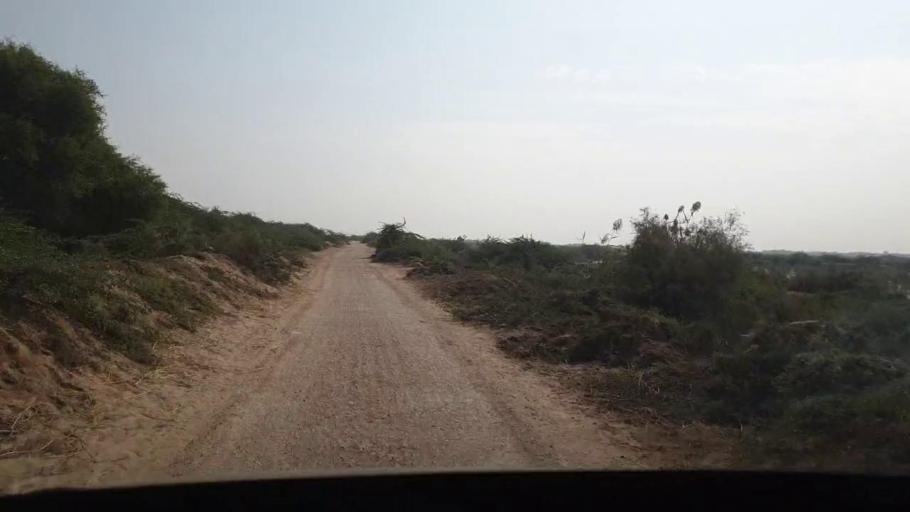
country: PK
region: Sindh
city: Chuhar Jamali
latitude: 24.2513
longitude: 67.9888
